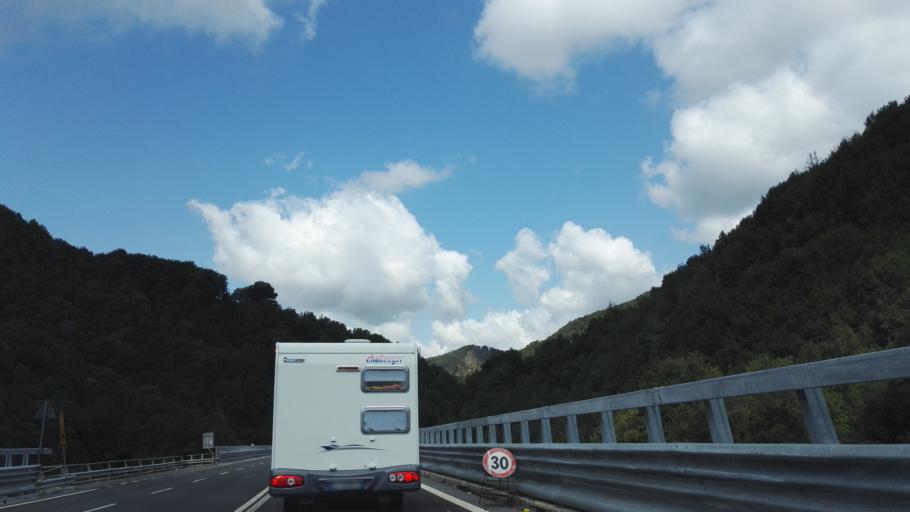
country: IT
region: Calabria
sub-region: Provincia di Reggio Calabria
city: Amato
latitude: 38.4067
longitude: 16.1499
